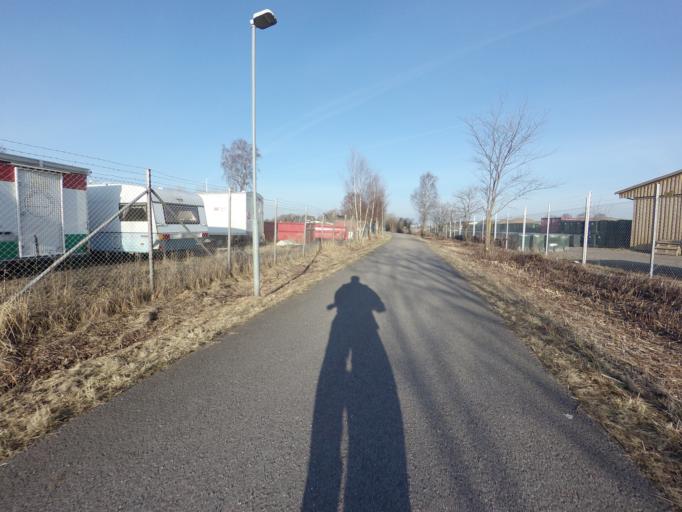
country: SE
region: Skane
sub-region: Hoganas Kommun
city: Hoganas
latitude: 56.2001
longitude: 12.5855
